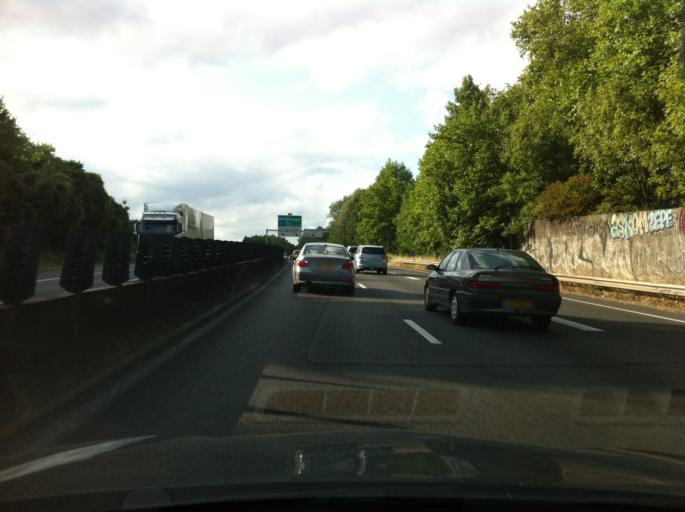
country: FR
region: Ile-de-France
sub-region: Departement de Seine-et-Marne
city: Brie-Comte-Robert
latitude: 48.6744
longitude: 2.6110
